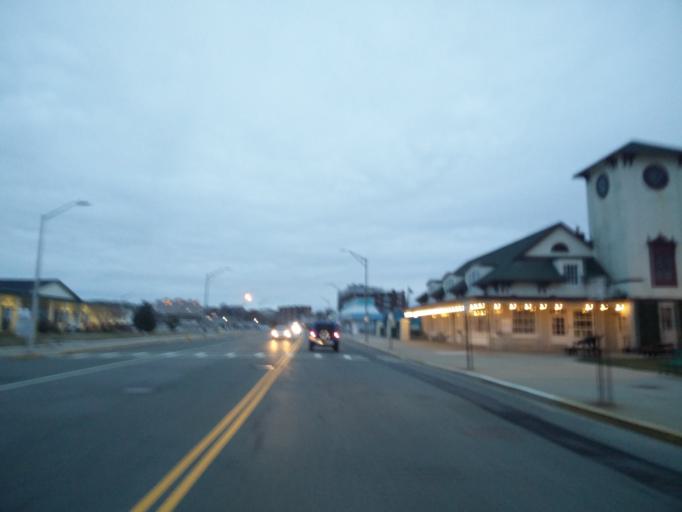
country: US
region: Massachusetts
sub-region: Plymouth County
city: Hingham
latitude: 42.2707
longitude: -70.8567
